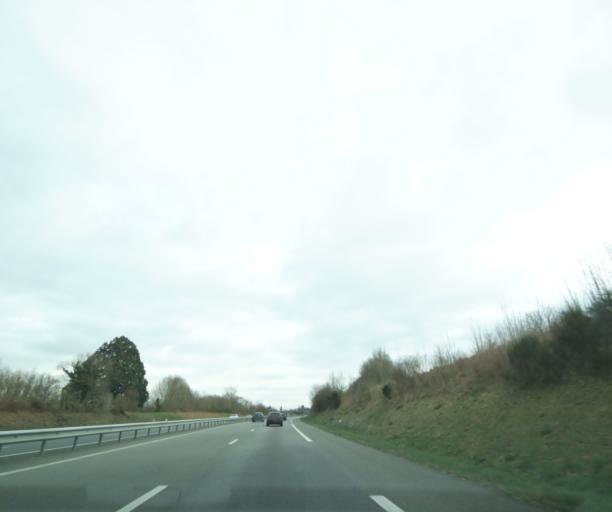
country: FR
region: Limousin
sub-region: Departement de la Haute-Vienne
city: Vicq-sur-Breuilh
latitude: 45.6558
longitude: 1.4016
